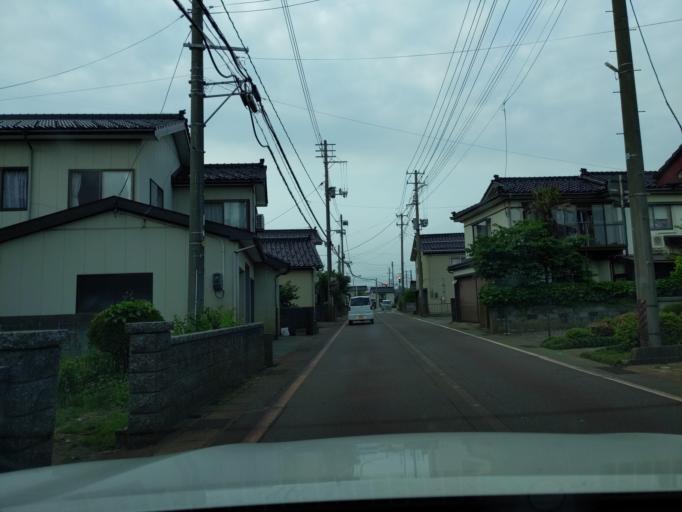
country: JP
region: Niigata
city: Kashiwazaki
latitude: 37.3873
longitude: 138.5785
